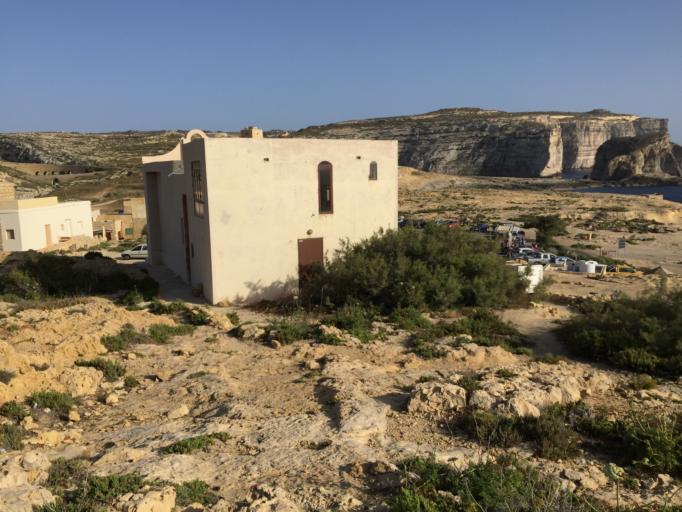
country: MT
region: Saint Lawrence
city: San Lawrenz
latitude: 36.0531
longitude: 14.1898
